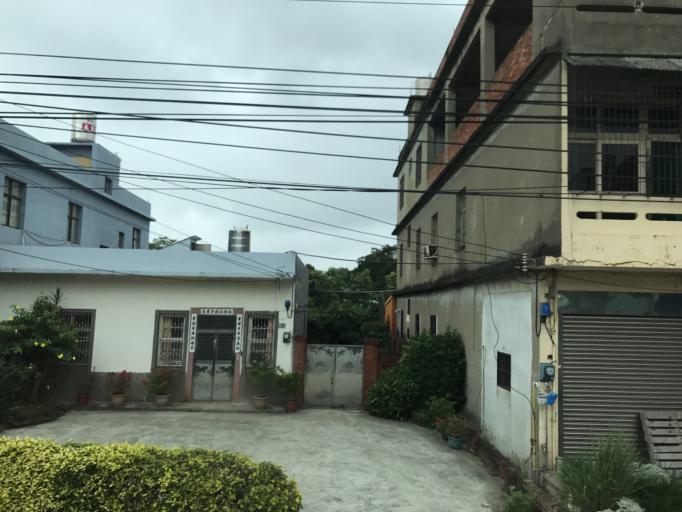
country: TW
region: Taiwan
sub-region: Hsinchu
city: Hsinchu
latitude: 24.8385
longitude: 120.9406
